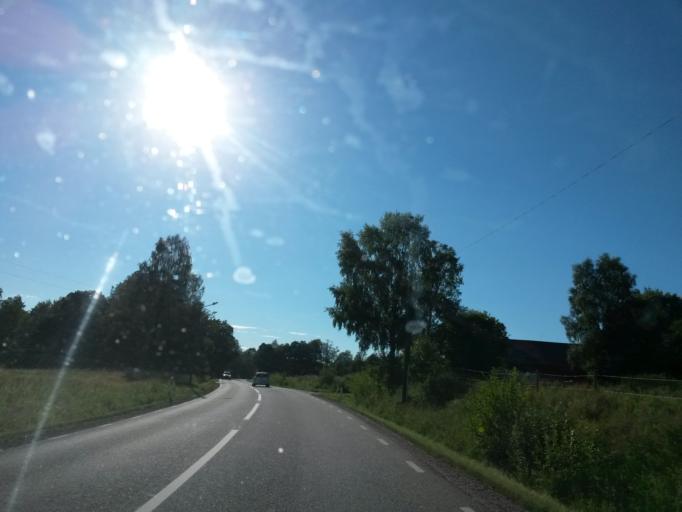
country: SE
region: Vaestra Goetaland
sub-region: Boras Kommun
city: Boras
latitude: 57.8375
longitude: 12.9836
